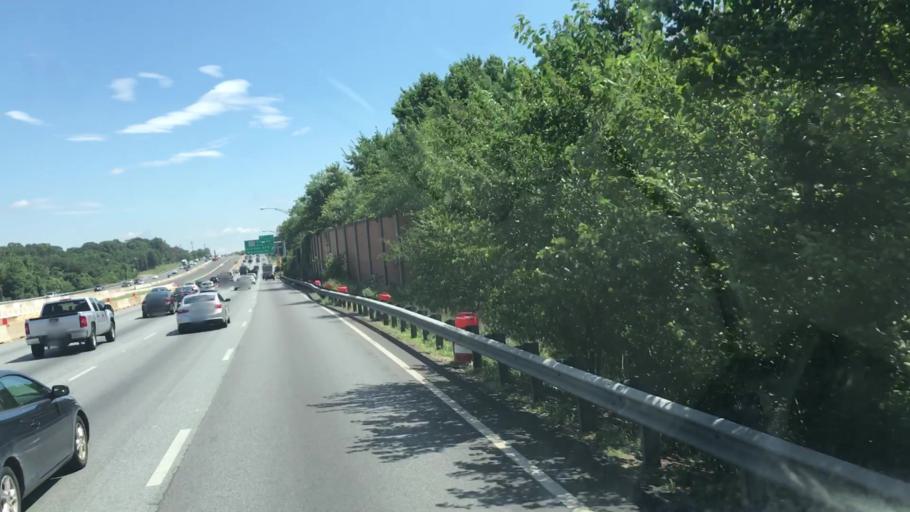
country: US
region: Maryland
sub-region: Prince George's County
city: Morningside
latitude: 38.8188
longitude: -76.8965
